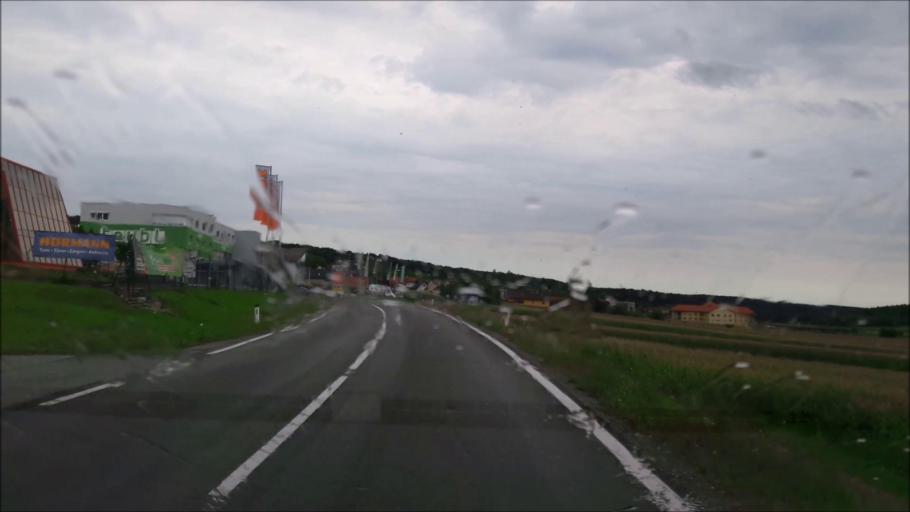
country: AT
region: Styria
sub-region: Politischer Bezirk Hartberg-Fuerstenfeld
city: Sankt Johann in der Haide
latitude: 47.2809
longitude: 16.0166
